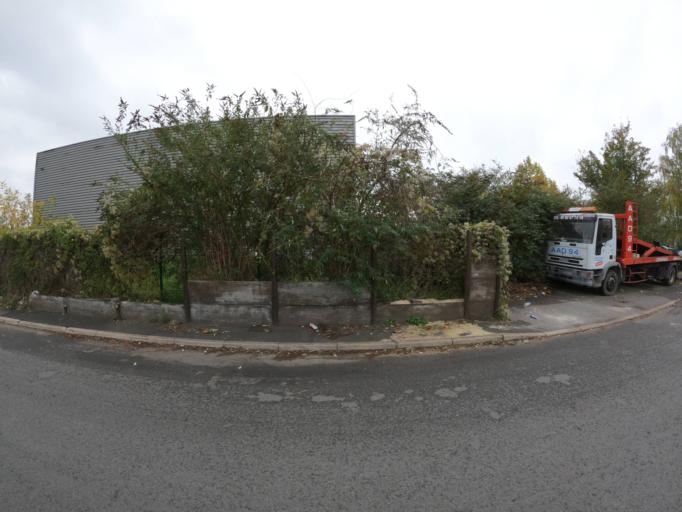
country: FR
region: Ile-de-France
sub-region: Departement du Val-de-Marne
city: Boissy-Saint-Leger
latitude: 48.7673
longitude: 2.5047
